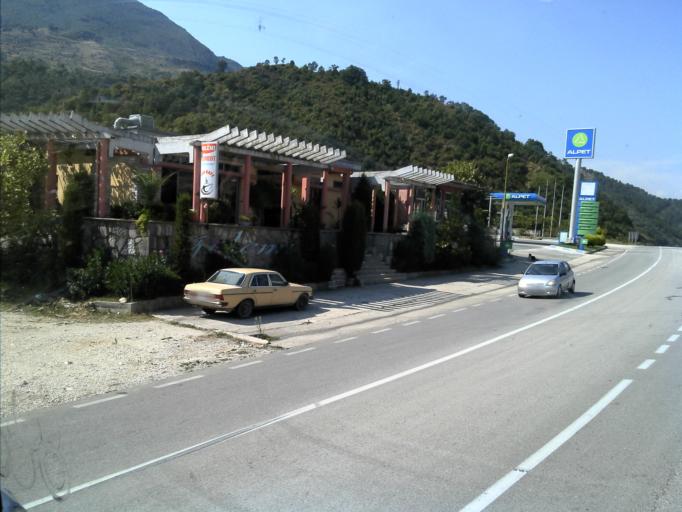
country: AL
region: Gjirokaster
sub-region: Rrethi i Gjirokastres
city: Picar
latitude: 40.2087
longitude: 20.0891
